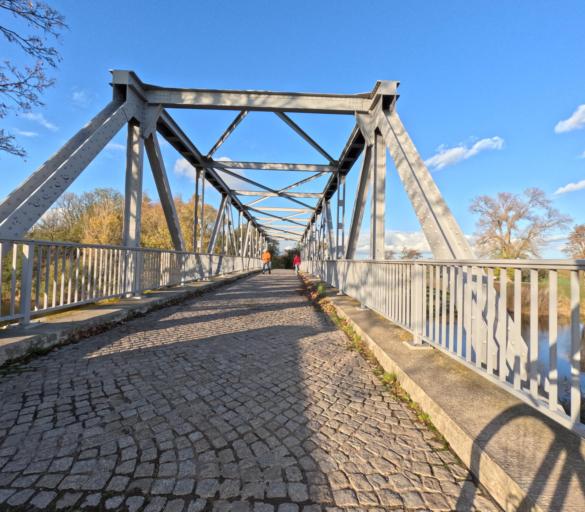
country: DE
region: Saxony
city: Schkeuditz
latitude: 51.3555
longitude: 12.2355
